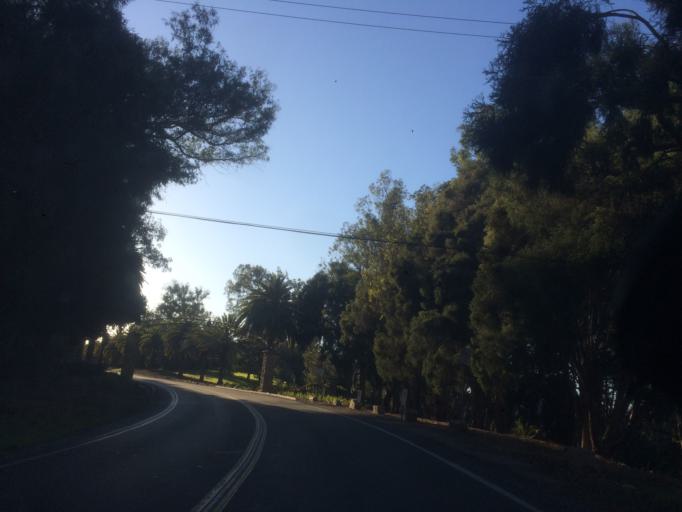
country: US
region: California
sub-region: Santa Barbara County
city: Mission Canyon
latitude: 34.4367
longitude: -119.7554
